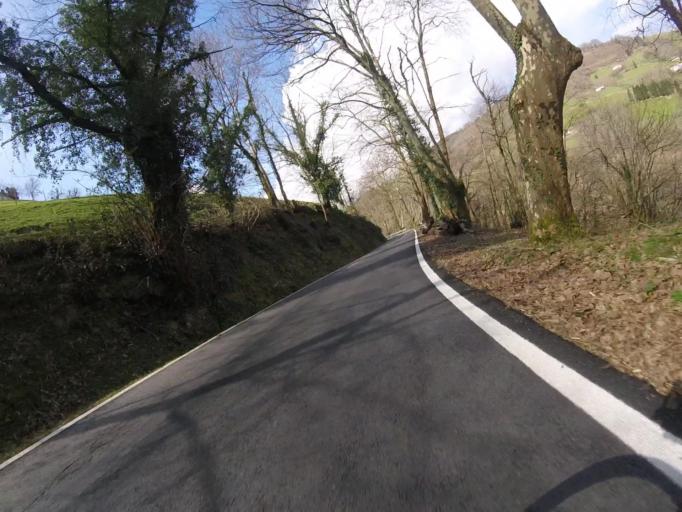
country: ES
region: Navarre
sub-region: Provincia de Navarra
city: Etxalar
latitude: 43.2462
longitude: -1.6200
